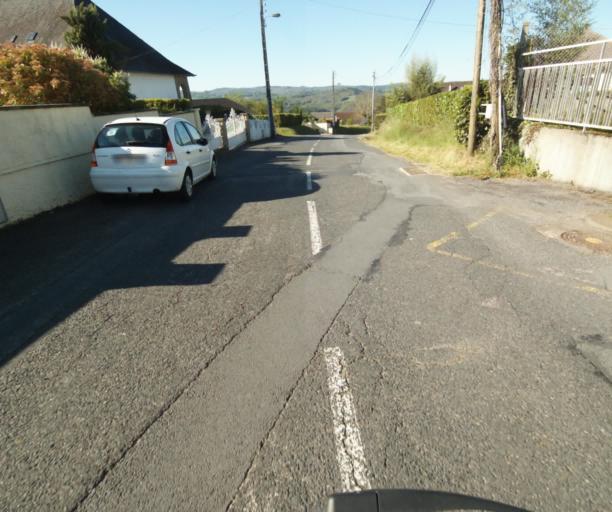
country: FR
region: Limousin
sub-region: Departement de la Correze
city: Tulle
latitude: 45.2674
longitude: 1.7855
